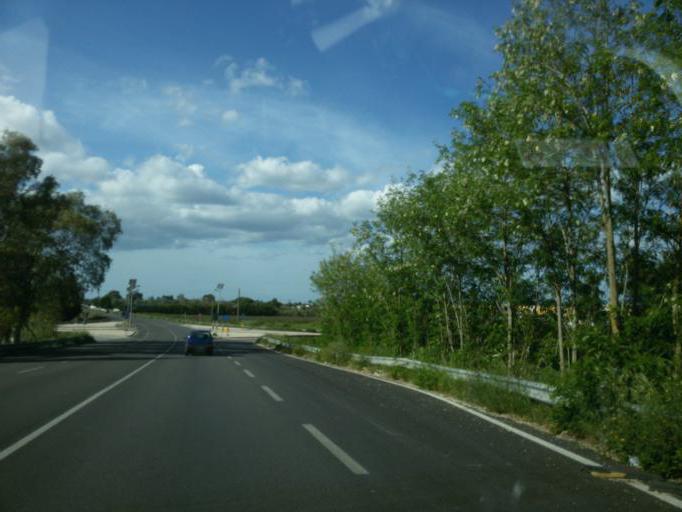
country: IT
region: Apulia
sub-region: Provincia di Brindisi
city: Mesagne
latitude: 40.5613
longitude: 17.7878
